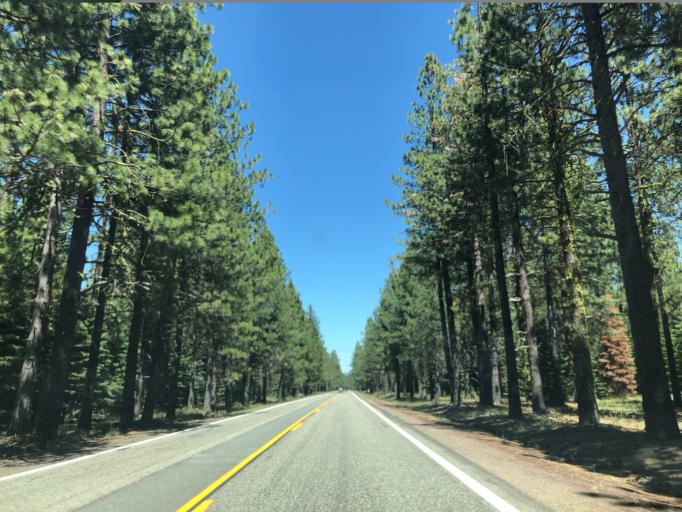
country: US
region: California
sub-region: Shasta County
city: Burney
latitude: 40.6028
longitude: -121.5296
